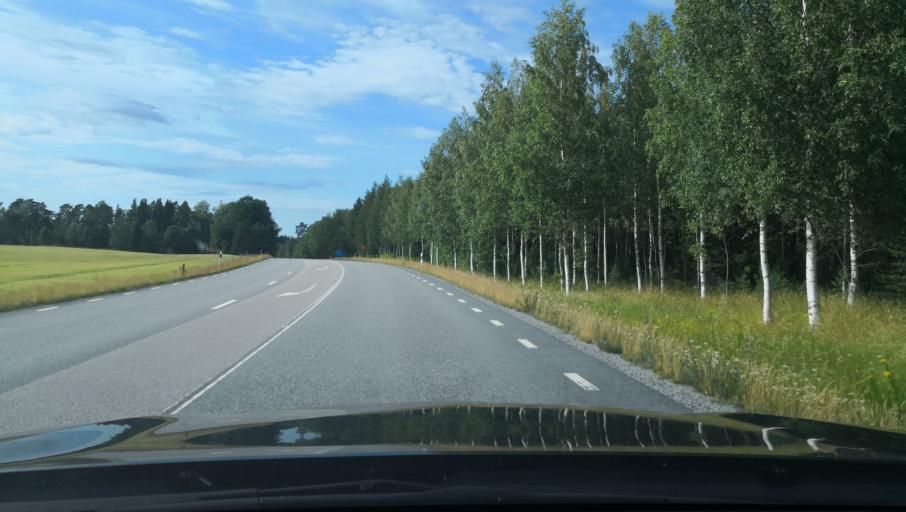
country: SE
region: Uppsala
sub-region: Habo Kommun
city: Balsta
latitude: 59.6214
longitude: 17.4974
